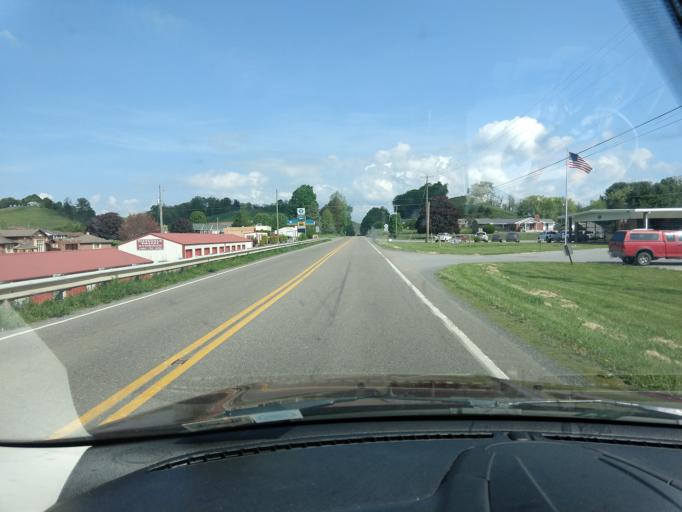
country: US
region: Virginia
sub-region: Russell County
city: Honaker
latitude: 36.9650
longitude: -81.9367
